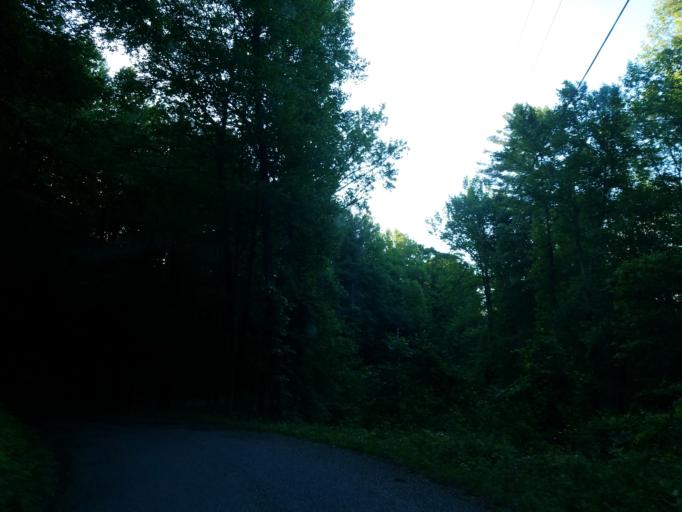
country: US
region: Georgia
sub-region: Lumpkin County
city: Dahlonega
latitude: 34.7070
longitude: -84.0140
